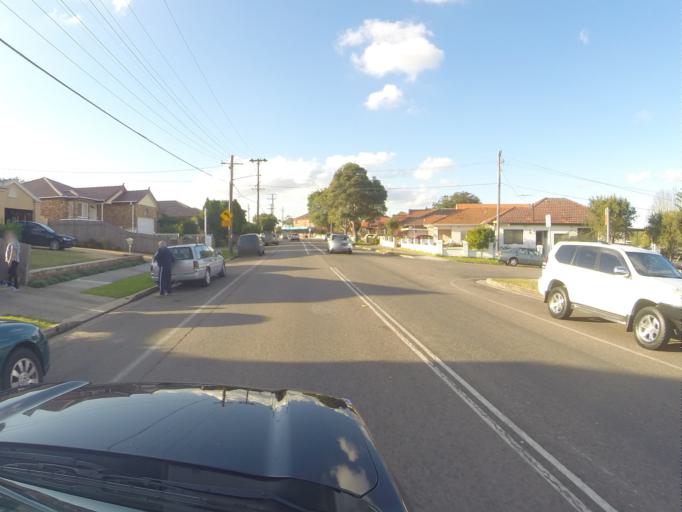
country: AU
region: New South Wales
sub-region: Rockdale
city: Bexley North
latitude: -33.9443
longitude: 151.1141
